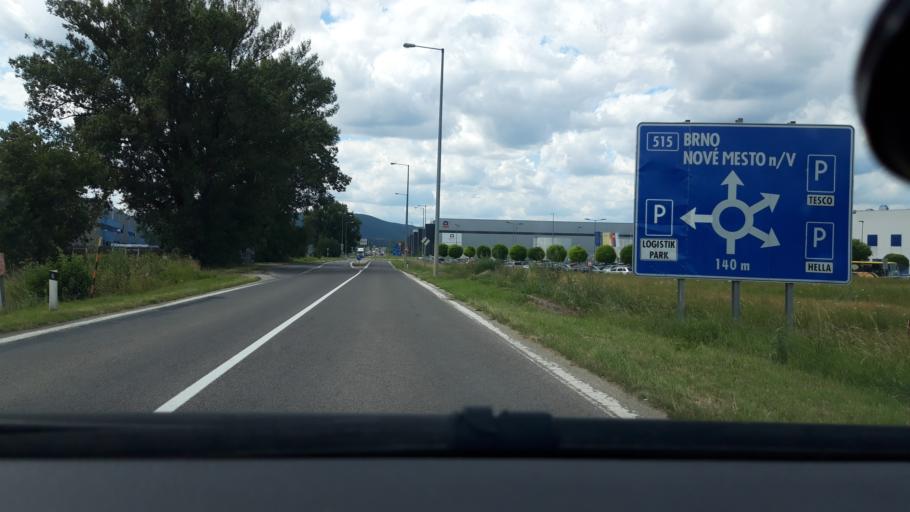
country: SK
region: Trenciansky
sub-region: Okres Nove Mesto nad Vahom
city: Nove Mesto nad Vahom
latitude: 48.7609
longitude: 17.8806
